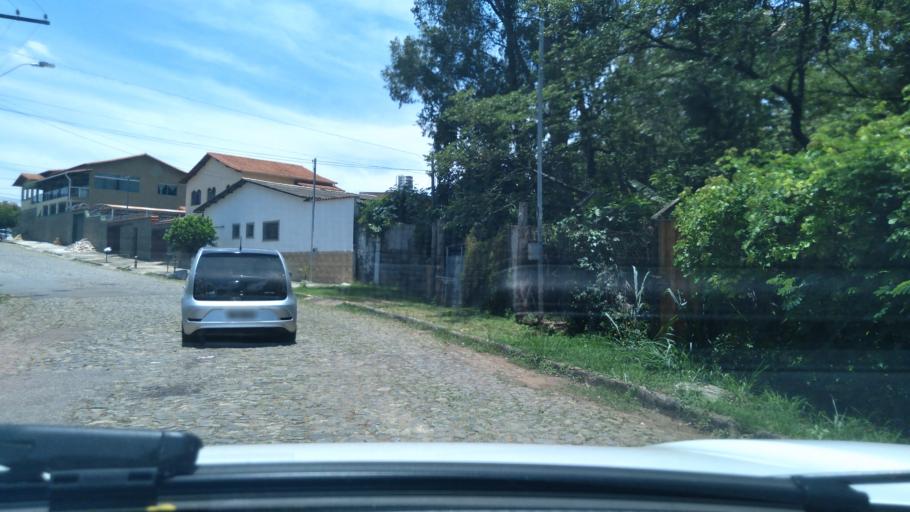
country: BR
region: Minas Gerais
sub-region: Contagem
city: Contagem
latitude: -19.9302
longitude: -44.0104
